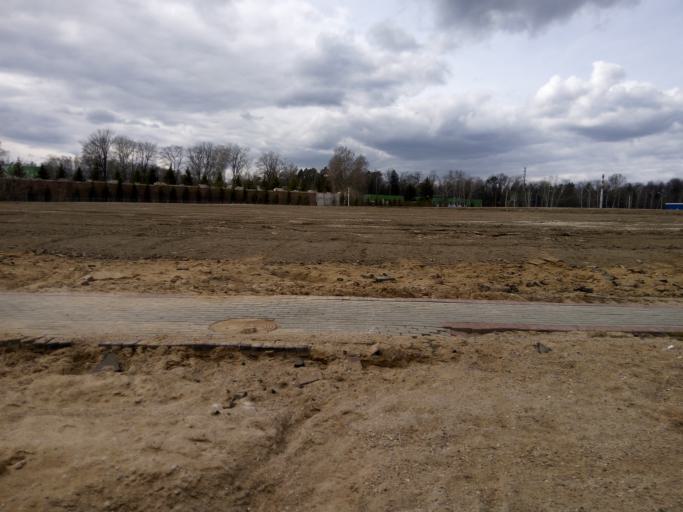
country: RU
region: Moskovskaya
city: Skolkovo
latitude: 55.6859
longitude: 37.3486
